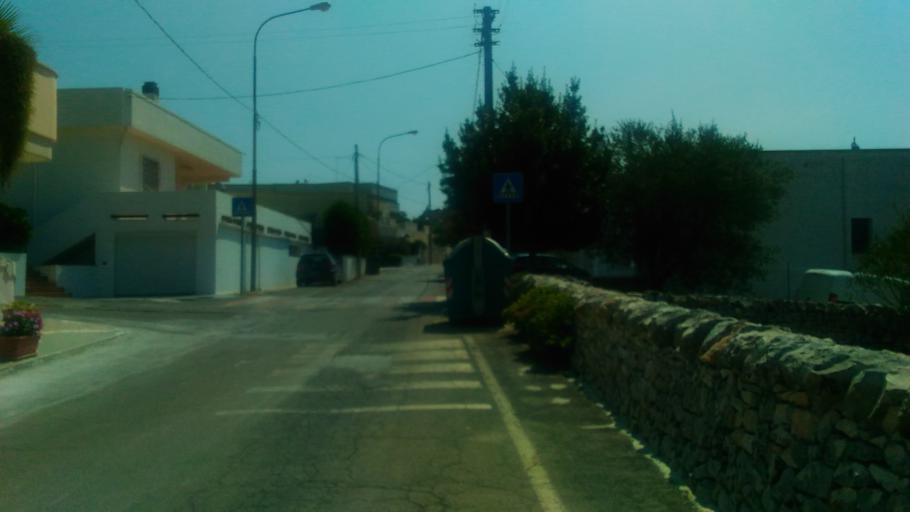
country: IT
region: Apulia
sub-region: Provincia di Bari
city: Locorotondo
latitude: 40.7481
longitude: 17.3739
